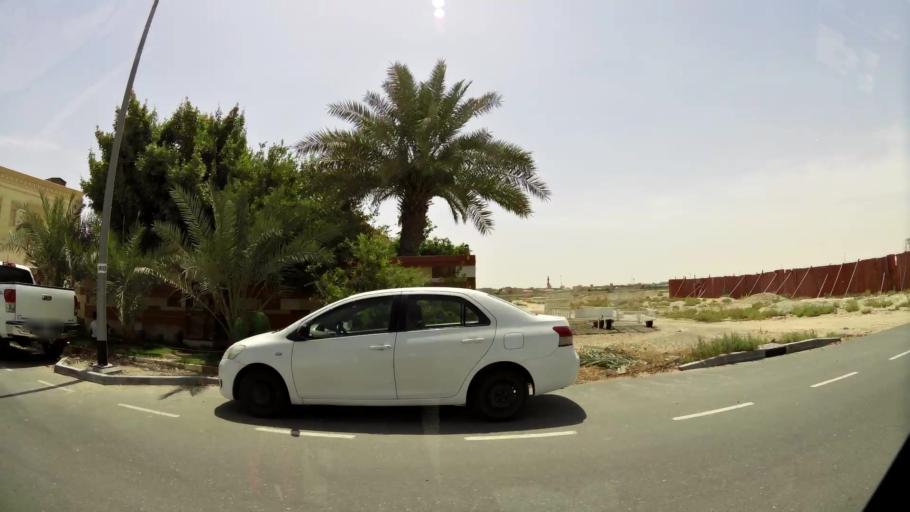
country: AE
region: Ash Shariqah
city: Sharjah
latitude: 25.1803
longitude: 55.4256
